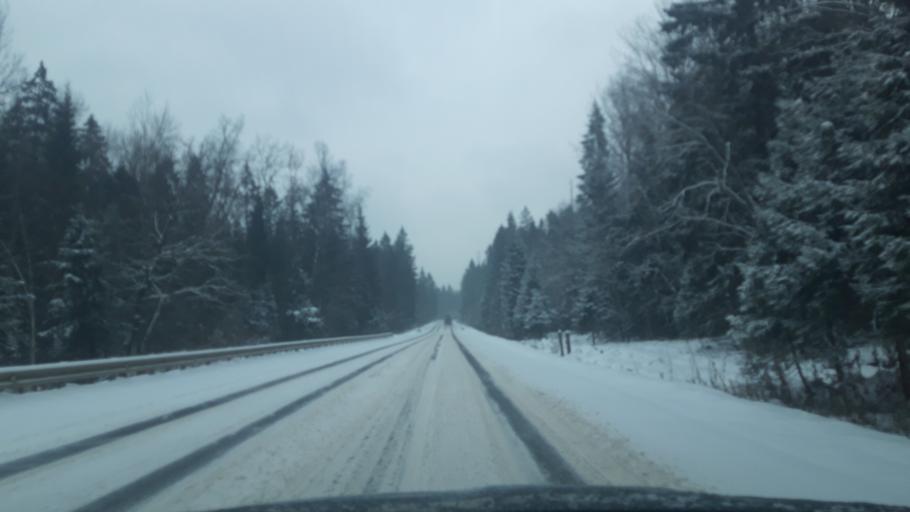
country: RU
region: Moskovskaya
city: Avtopoligon
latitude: 56.2831
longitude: 37.3770
